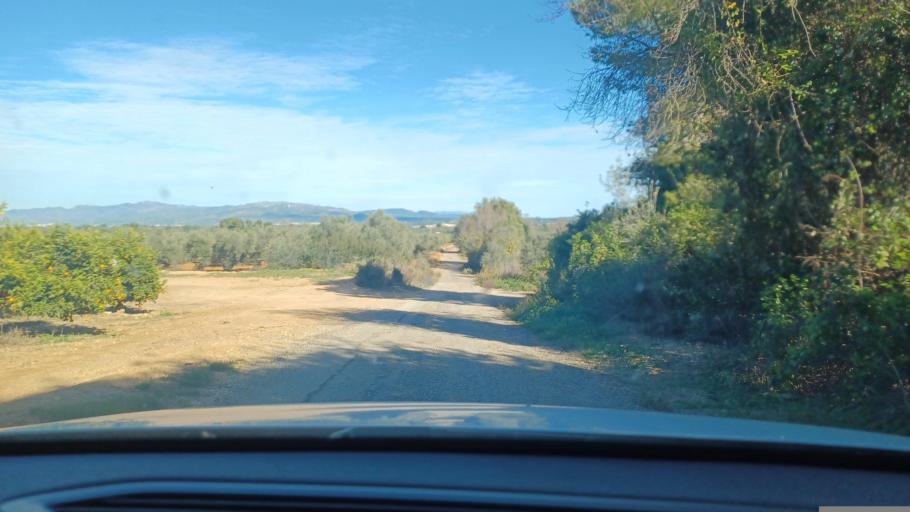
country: ES
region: Catalonia
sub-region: Provincia de Tarragona
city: Santa Barbara
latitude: 40.6874
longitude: 0.5019
